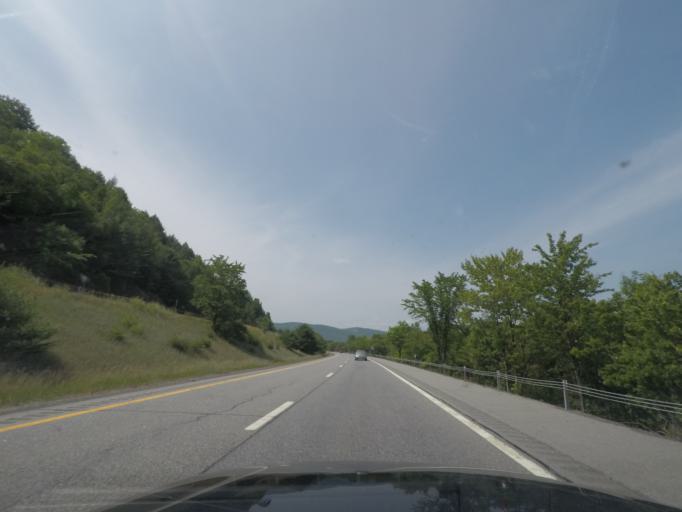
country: US
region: New York
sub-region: Warren County
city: Warrensburg
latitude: 43.7139
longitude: -73.8108
